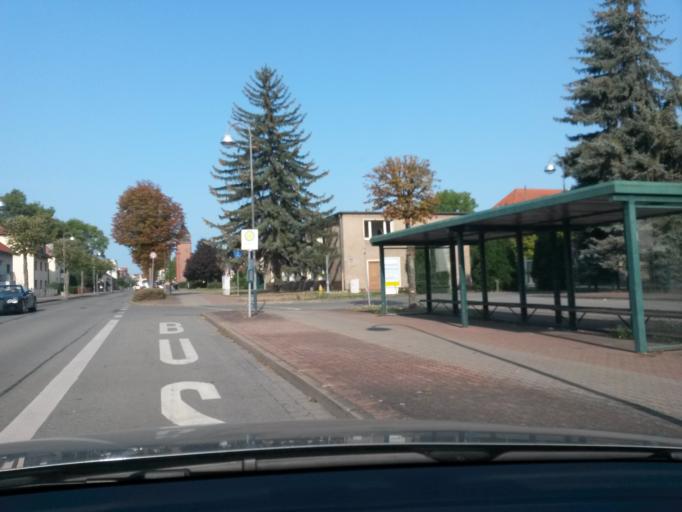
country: DE
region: Saxony-Anhalt
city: Tangerhutte
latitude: 52.4336
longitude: 11.8190
